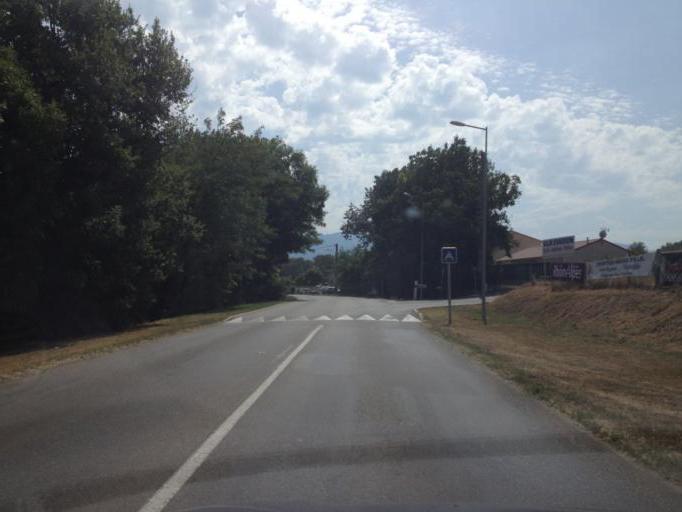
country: FR
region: Rhone-Alpes
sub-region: Departement de la Drome
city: Chatuzange-le-Goubet
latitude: 45.0120
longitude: 5.0860
